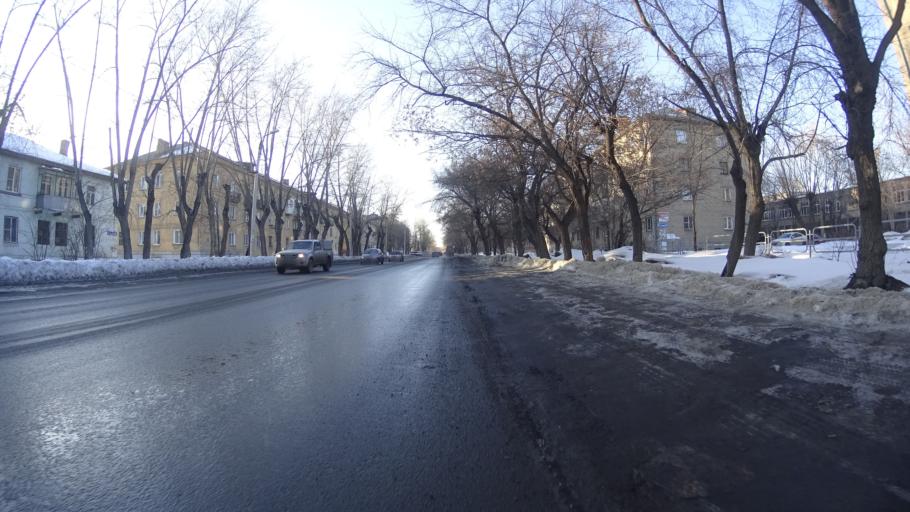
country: RU
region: Chelyabinsk
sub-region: Gorod Chelyabinsk
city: Chelyabinsk
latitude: 55.1277
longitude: 61.4703
